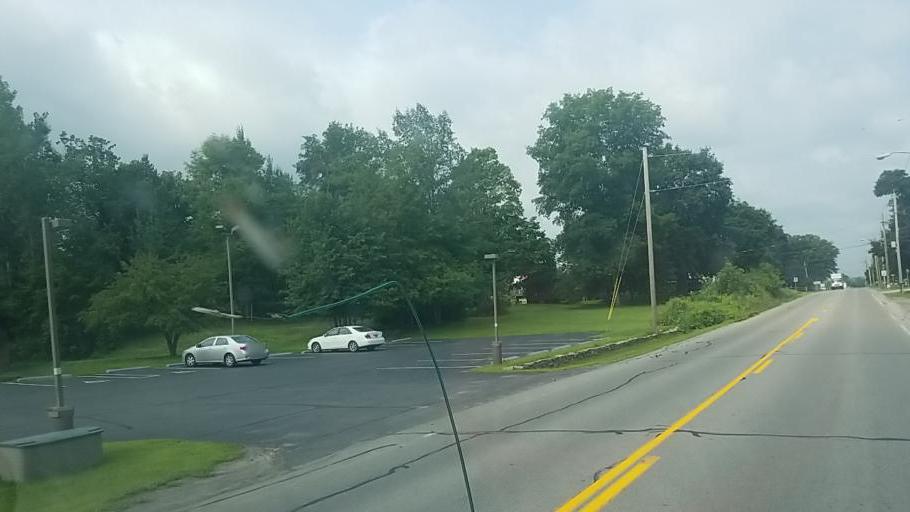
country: US
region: New York
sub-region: Montgomery County
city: Canajoharie
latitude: 42.9138
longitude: -74.5837
